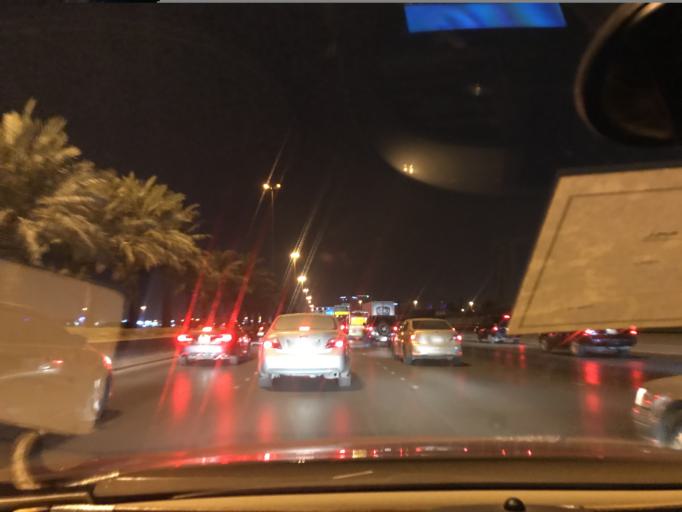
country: SA
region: Ar Riyad
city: Riyadh
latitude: 24.7701
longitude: 46.7337
